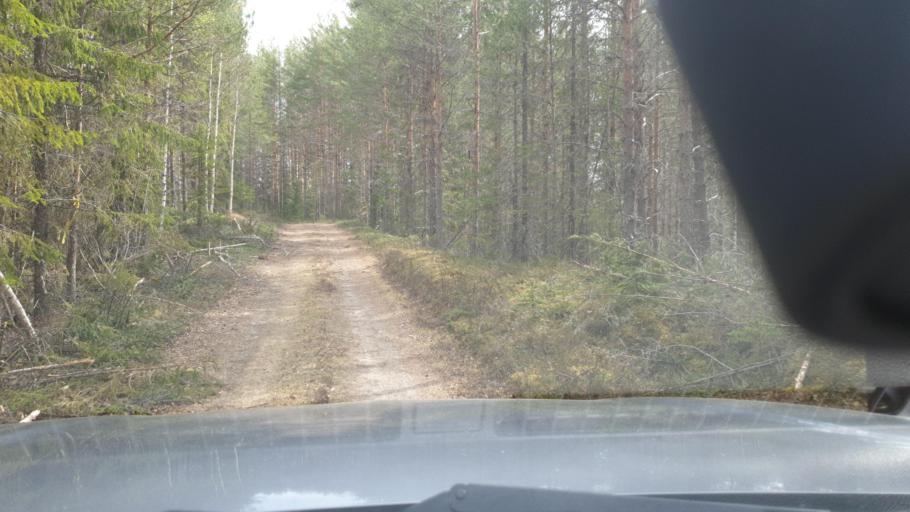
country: SE
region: Vaesternorrland
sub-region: Ange Kommun
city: Ange
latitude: 62.1894
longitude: 15.6037
